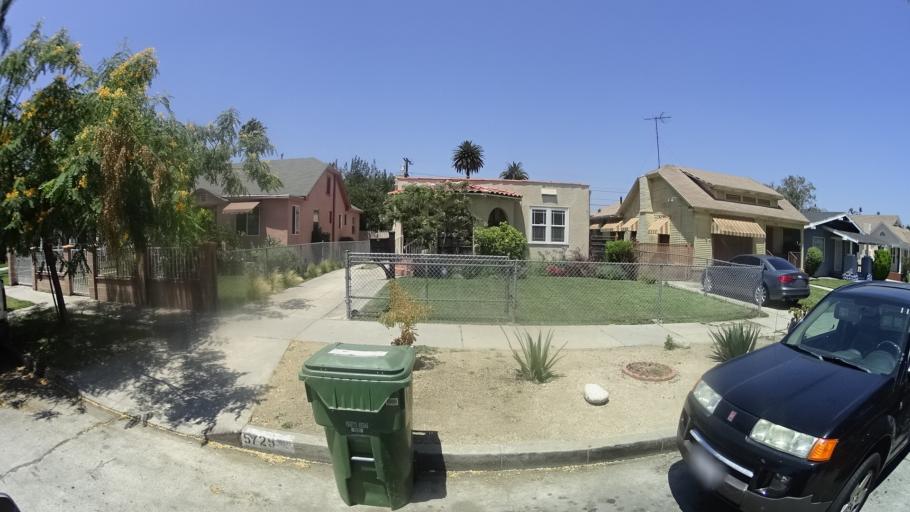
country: US
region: California
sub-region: Los Angeles County
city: View Park-Windsor Hills
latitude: 33.9901
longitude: -118.3215
